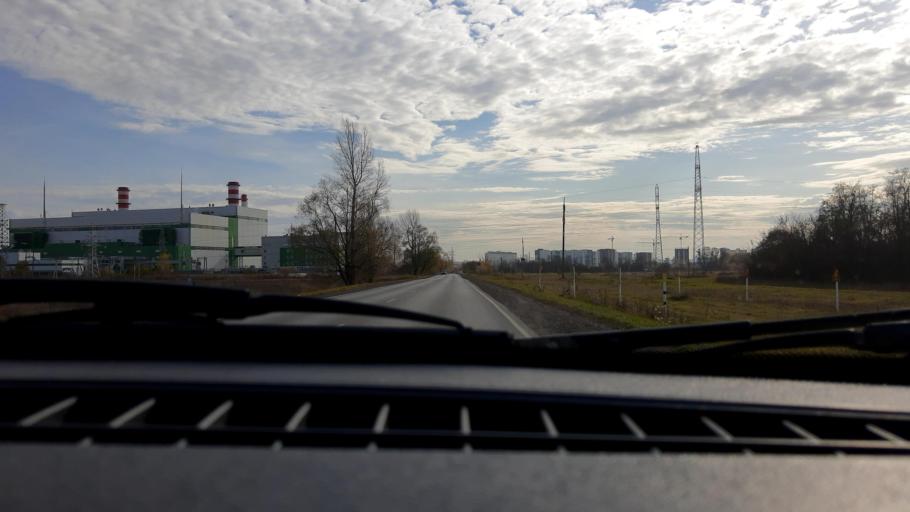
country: RU
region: Bashkortostan
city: Mikhaylovka
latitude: 54.8028
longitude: 55.8296
